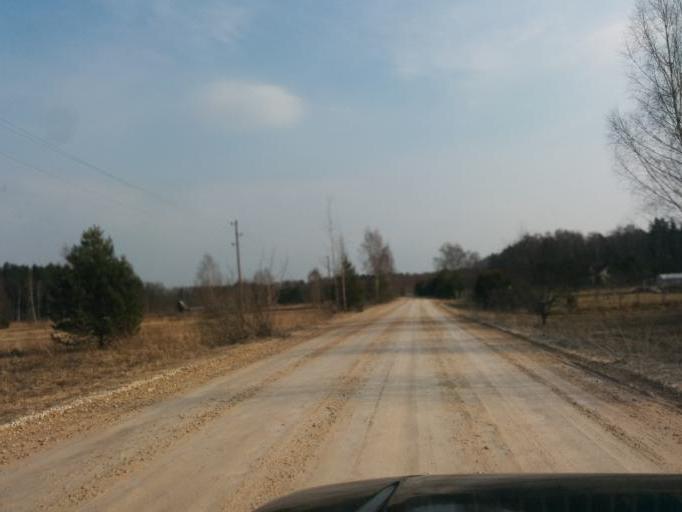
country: LV
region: Olaine
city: Olaine
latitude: 56.7922
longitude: 23.9921
